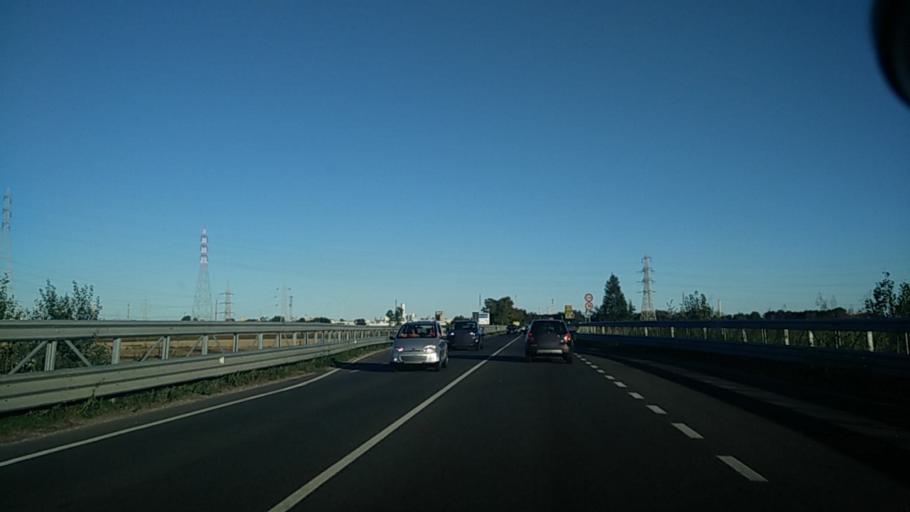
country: IT
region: Veneto
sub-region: Provincia di Venezia
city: Fornase
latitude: 45.4541
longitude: 12.1969
